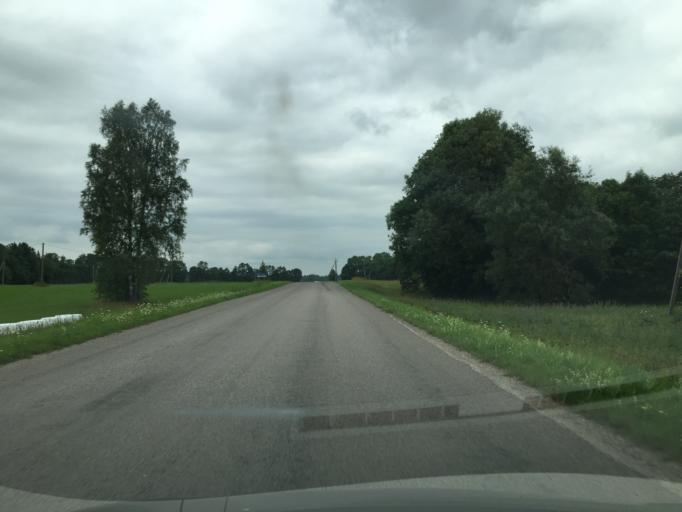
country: EE
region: Raplamaa
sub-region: Jaervakandi vald
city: Jarvakandi
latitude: 58.7963
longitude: 24.9281
